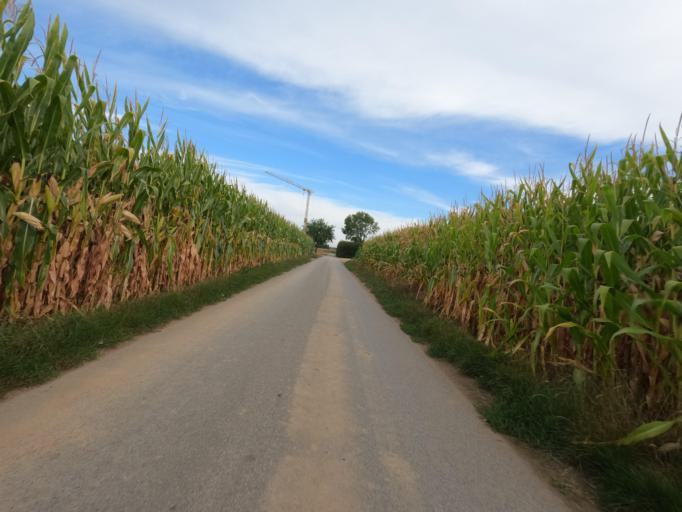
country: NL
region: Limburg
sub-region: Gemeente Roerdalen
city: Vlodrop
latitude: 51.1052
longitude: 6.0857
